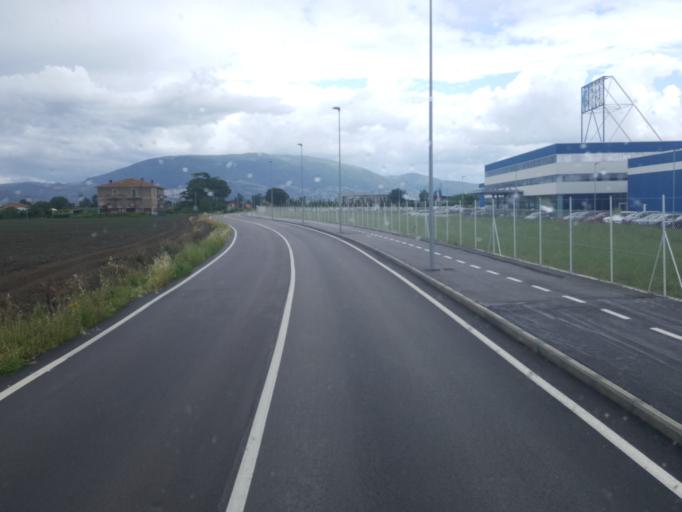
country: IT
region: Umbria
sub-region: Provincia di Perugia
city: Ospedalicchio
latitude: 43.0711
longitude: 12.5037
